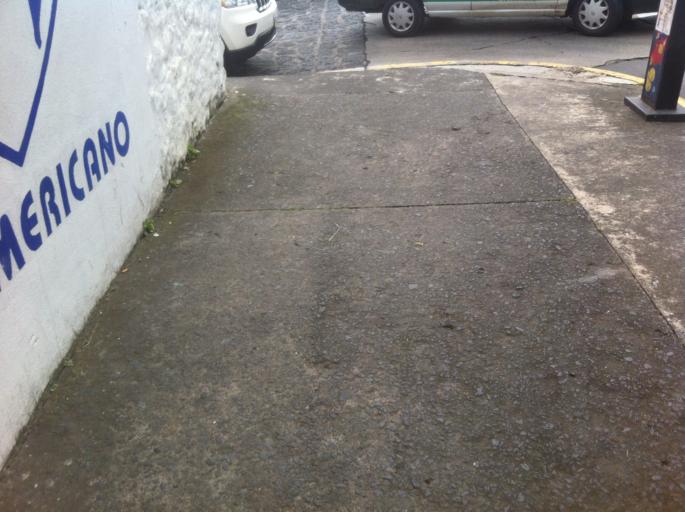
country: MX
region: Veracruz
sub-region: Xalapa
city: Xalapa de Enriquez
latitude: 19.5301
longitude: -96.9131
